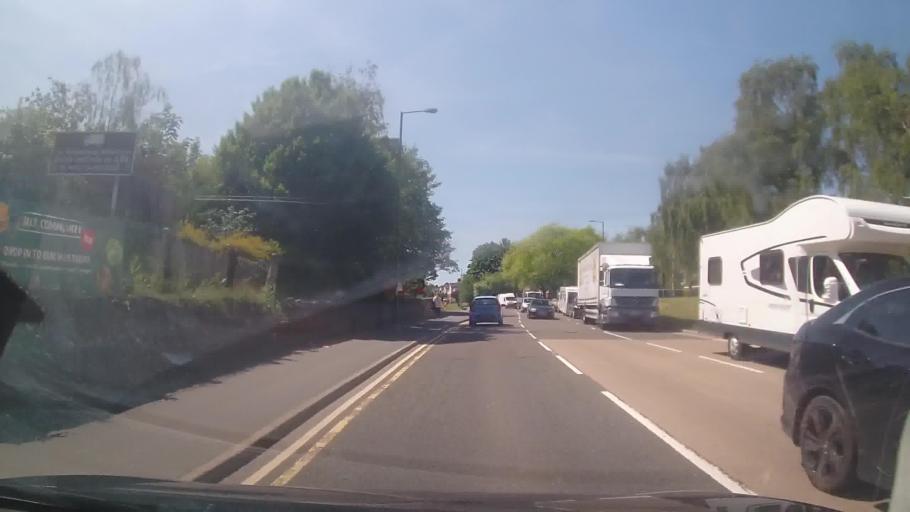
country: GB
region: England
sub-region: Herefordshire
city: Hereford
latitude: 52.0480
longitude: -2.7194
